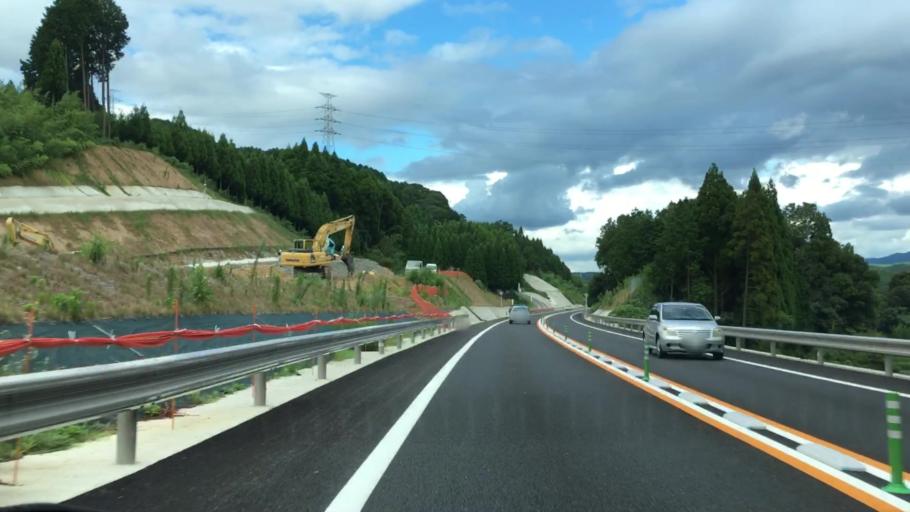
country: JP
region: Saga Prefecture
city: Imaricho-ko
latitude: 33.3137
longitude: 129.9185
